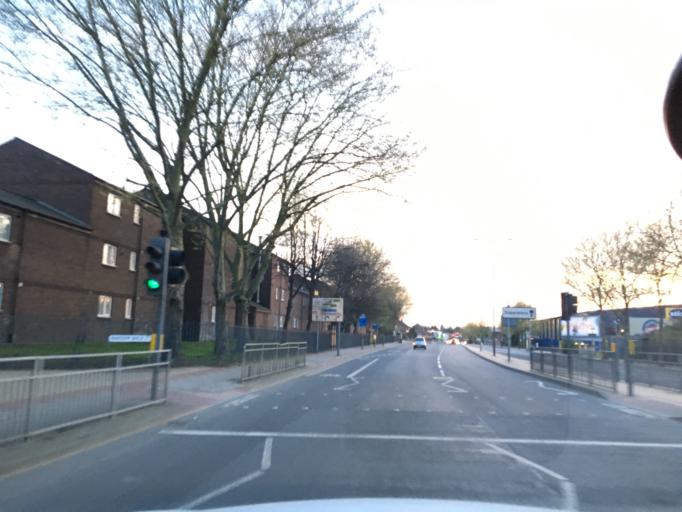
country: GB
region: England
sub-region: Greater London
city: Woolwich
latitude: 51.4885
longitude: 0.0344
